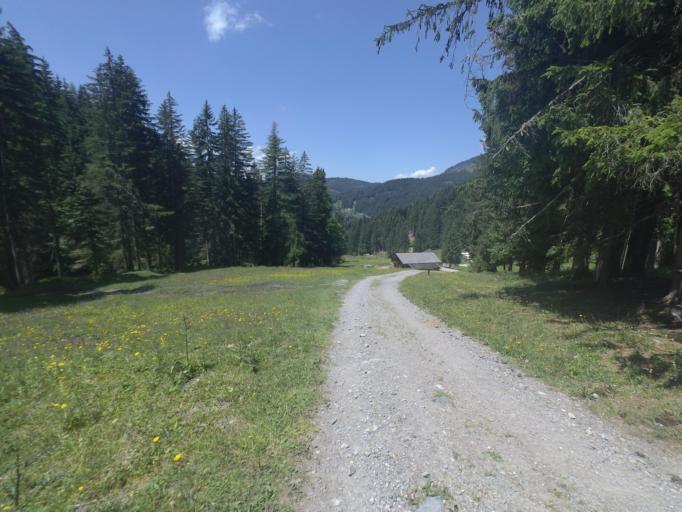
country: AT
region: Salzburg
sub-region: Politischer Bezirk Zell am See
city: Dienten am Hochkonig
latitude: 47.4111
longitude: 12.9959
